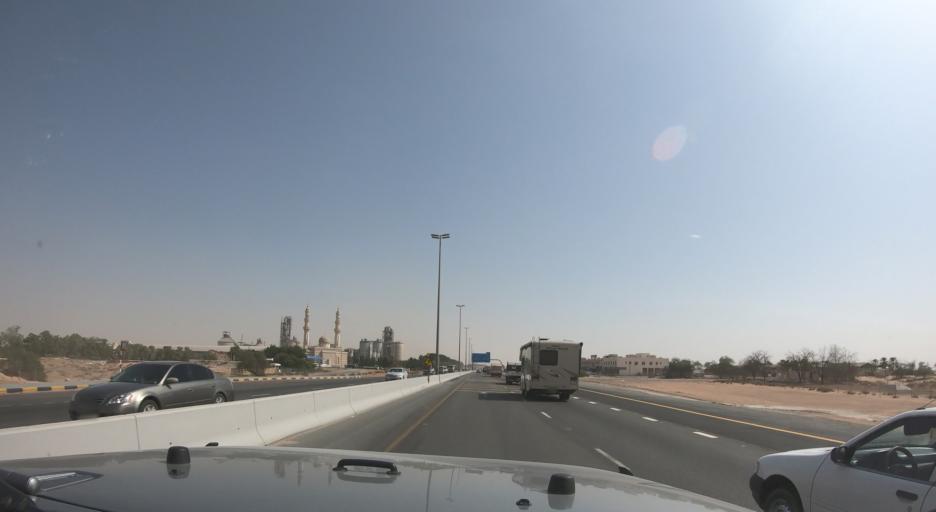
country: AE
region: Ash Shariqah
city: Sharjah
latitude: 25.2969
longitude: 55.6074
